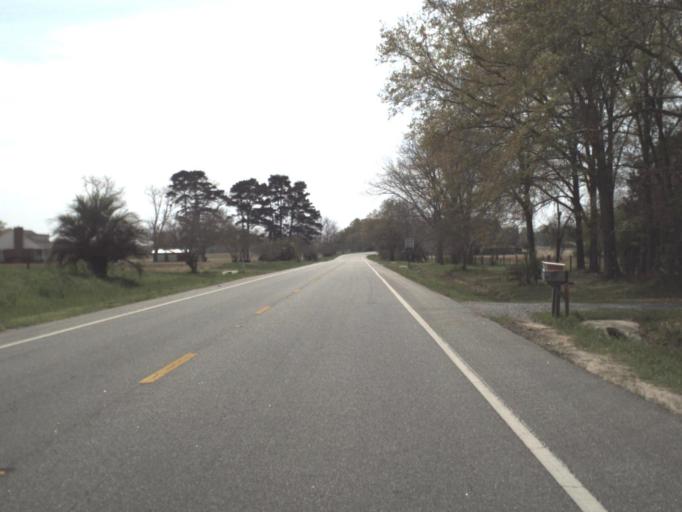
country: US
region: Florida
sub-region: Jackson County
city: Graceville
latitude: 30.9941
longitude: -85.4793
